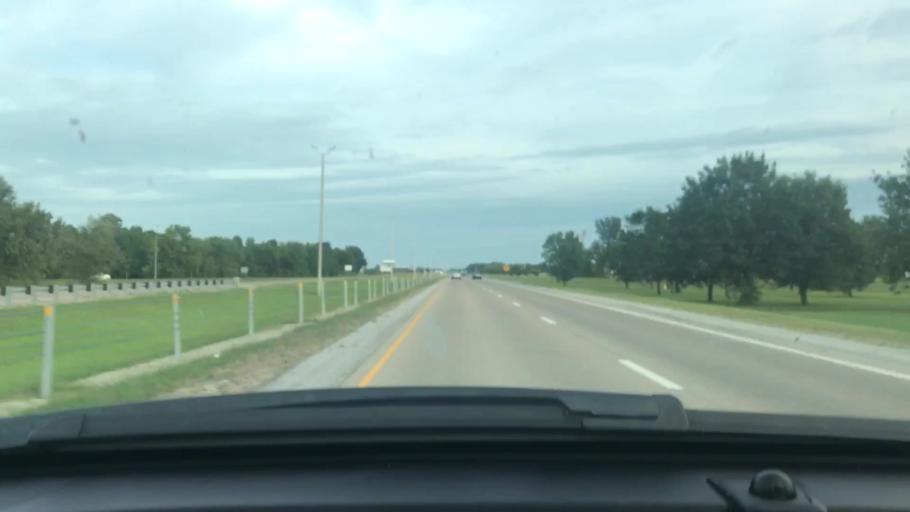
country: US
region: Arkansas
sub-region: Craighead County
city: Bay
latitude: 35.8012
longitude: -90.6243
